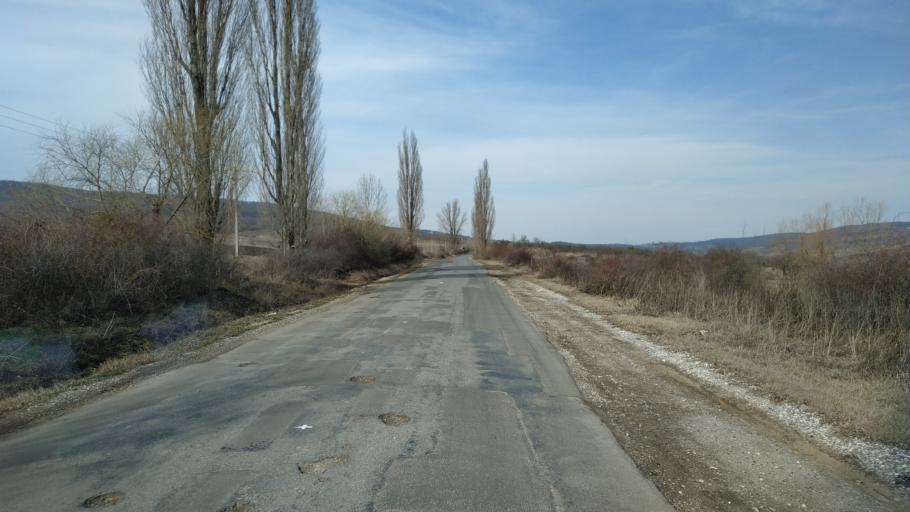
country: MD
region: Nisporeni
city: Nisporeni
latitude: 47.1703
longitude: 28.0928
